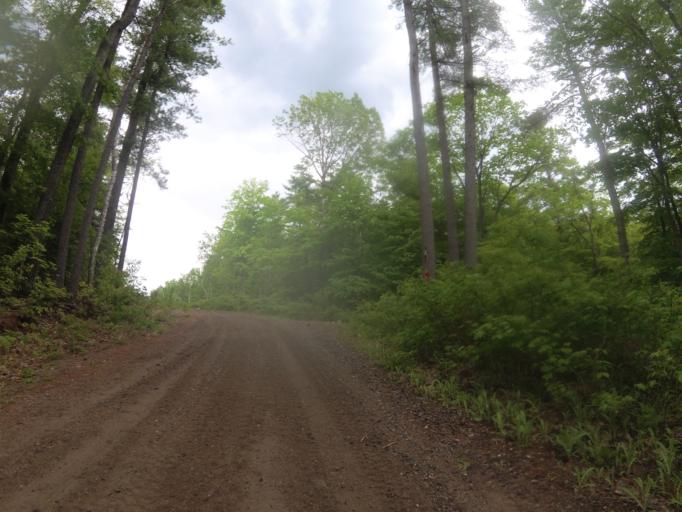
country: CA
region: Ontario
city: Renfrew
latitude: 45.1173
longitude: -76.8222
